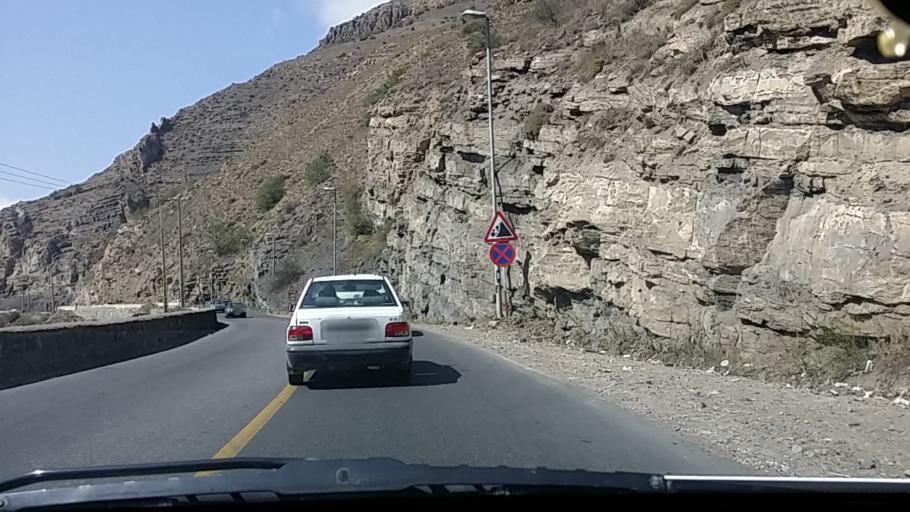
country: IR
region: Mazandaran
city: Chalus
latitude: 36.2465
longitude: 51.2971
